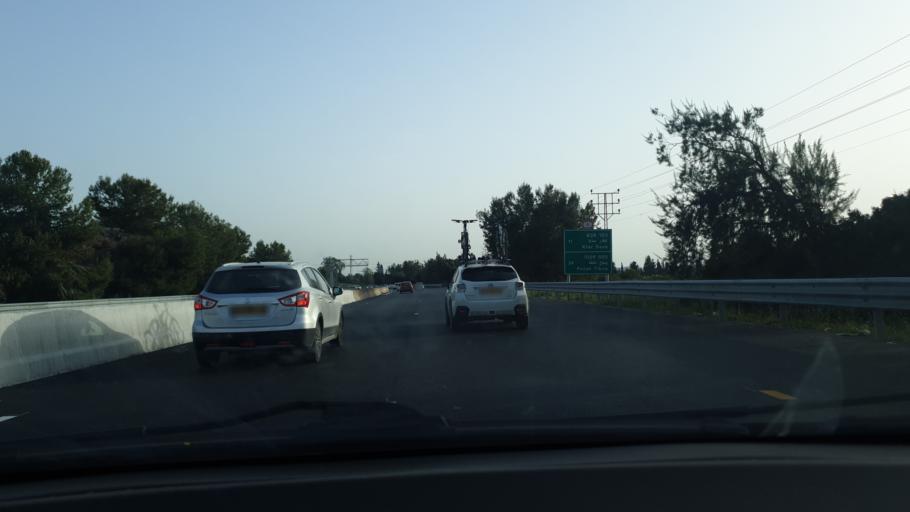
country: IL
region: Central District
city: Tel Mond
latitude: 32.2290
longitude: 34.8834
